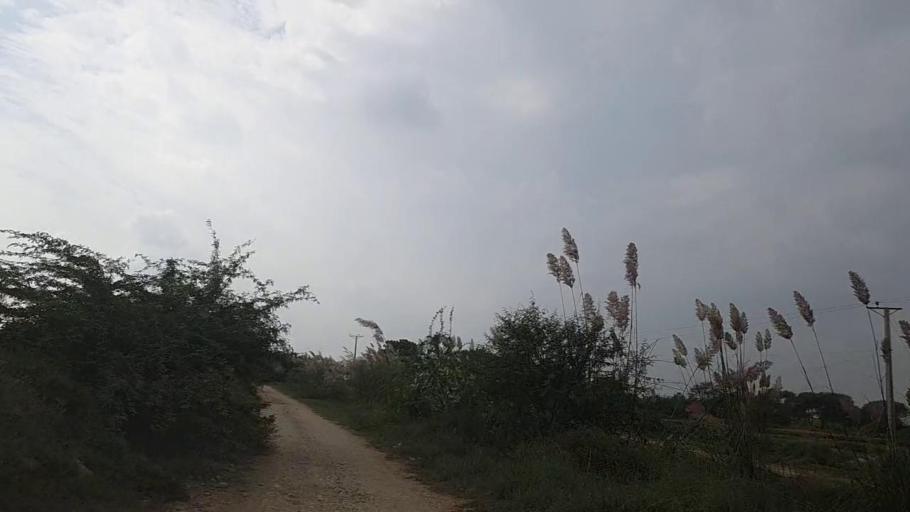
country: PK
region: Sindh
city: Mirpur Batoro
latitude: 24.5997
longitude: 68.1339
